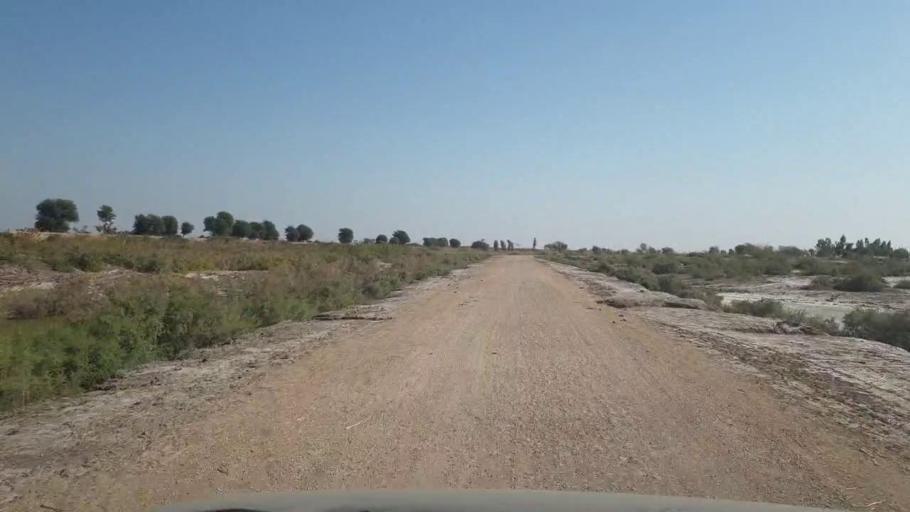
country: PK
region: Sindh
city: Samaro
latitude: 25.3746
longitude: 69.3304
